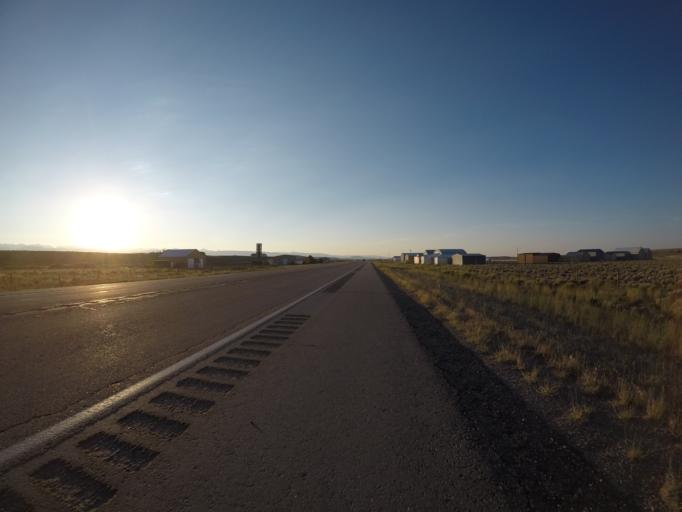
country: US
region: Wyoming
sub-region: Sublette County
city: Pinedale
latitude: 42.8004
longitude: -109.8079
